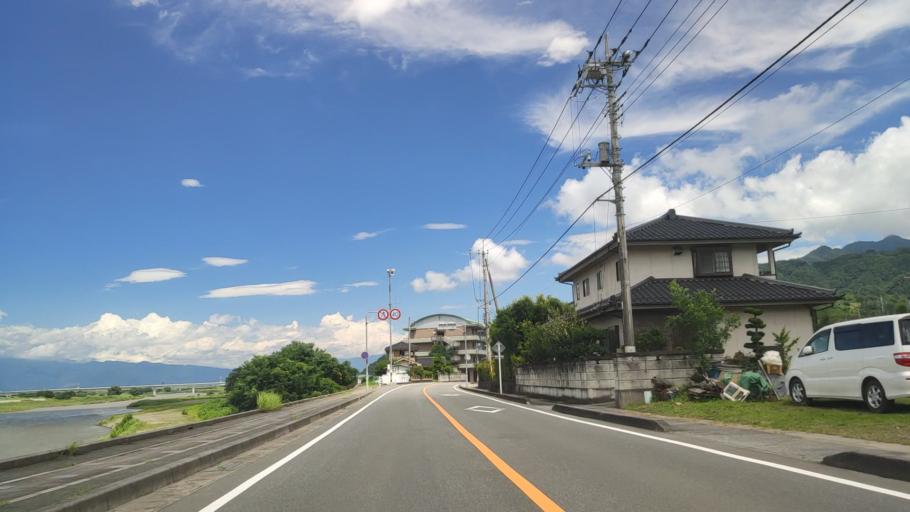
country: JP
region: Yamanashi
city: Ryuo
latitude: 35.5399
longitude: 138.4629
